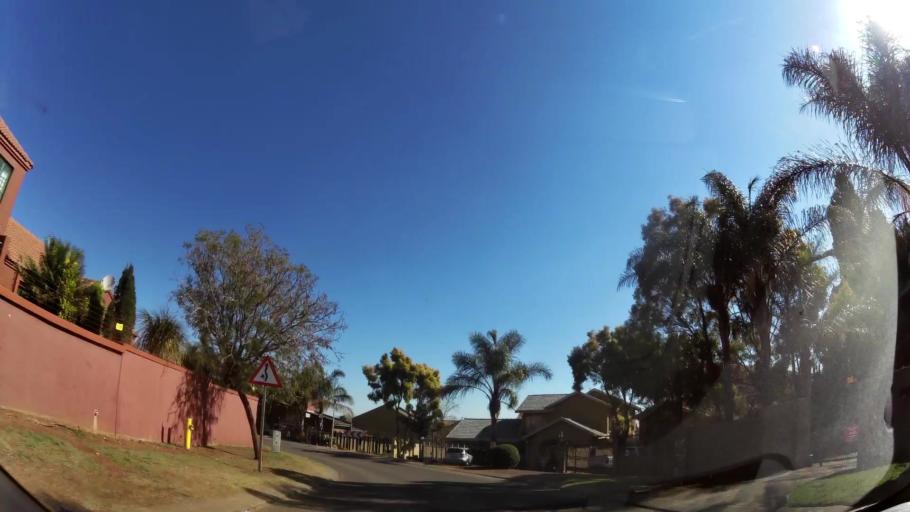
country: ZA
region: Gauteng
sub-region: City of Tshwane Metropolitan Municipality
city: Centurion
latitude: -25.8626
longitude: 28.1780
